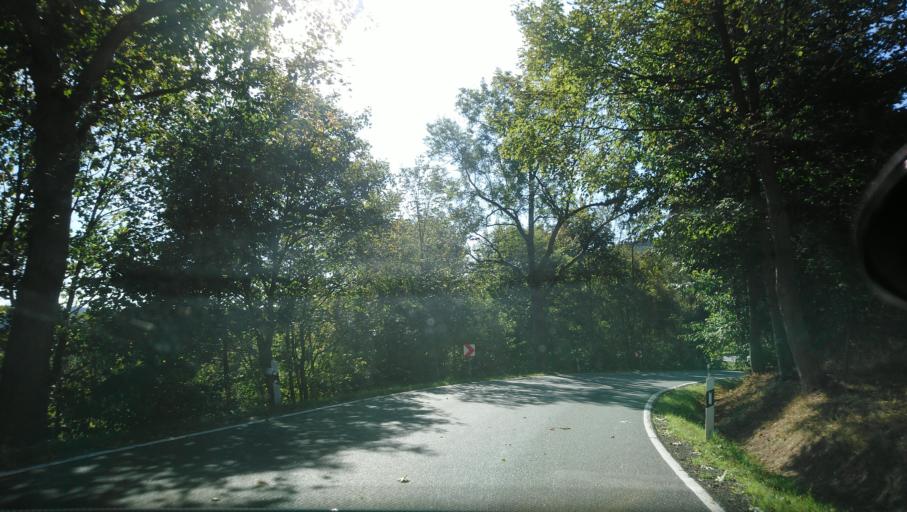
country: DE
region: Saxony
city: Konigswalde
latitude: 50.5461
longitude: 13.0341
